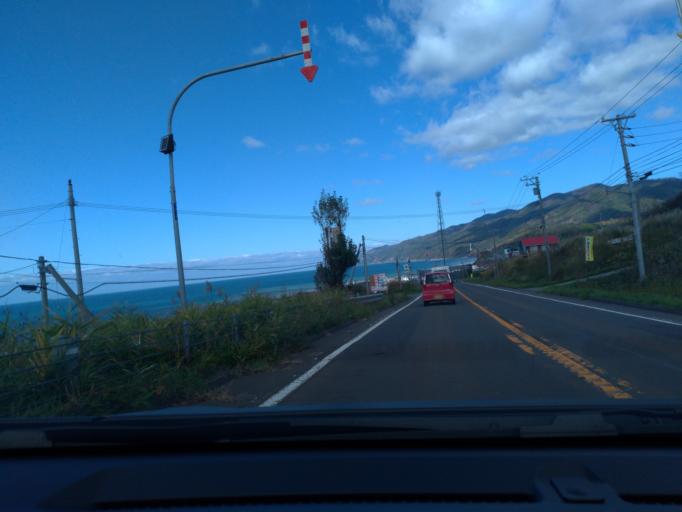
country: JP
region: Hokkaido
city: Ishikari
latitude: 43.3919
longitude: 141.4330
